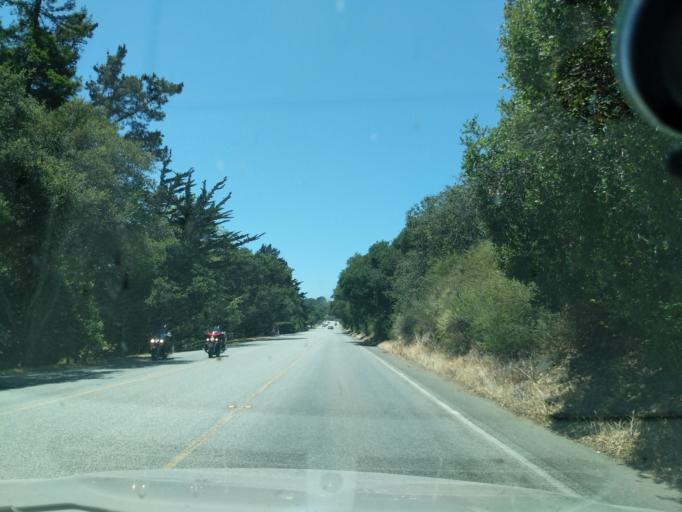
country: US
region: California
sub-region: Monterey County
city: Del Rey Oaks
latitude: 36.5325
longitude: -121.8427
